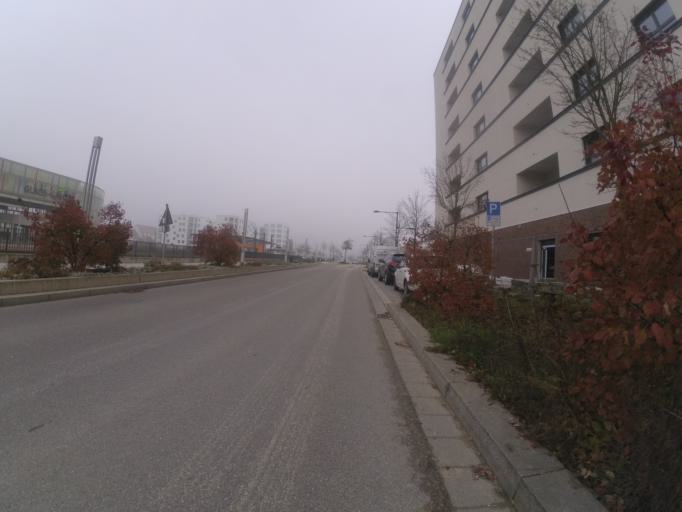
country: DE
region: Bavaria
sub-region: Swabia
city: Neu-Ulm
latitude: 48.3938
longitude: 10.0067
